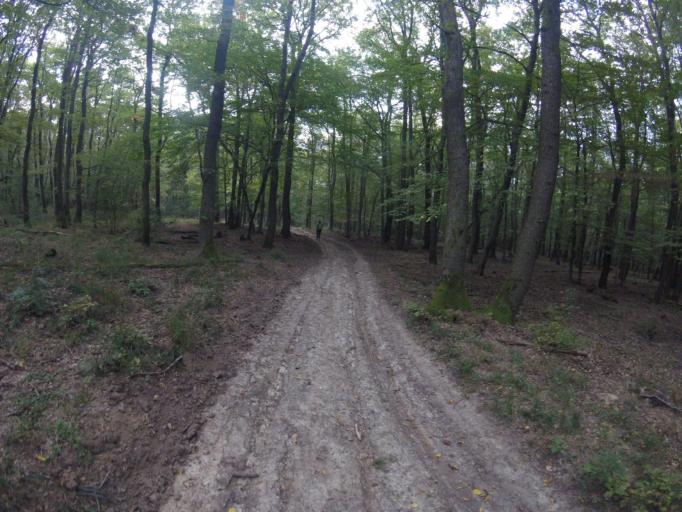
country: HU
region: Pest
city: Szob
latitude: 47.8010
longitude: 18.8241
